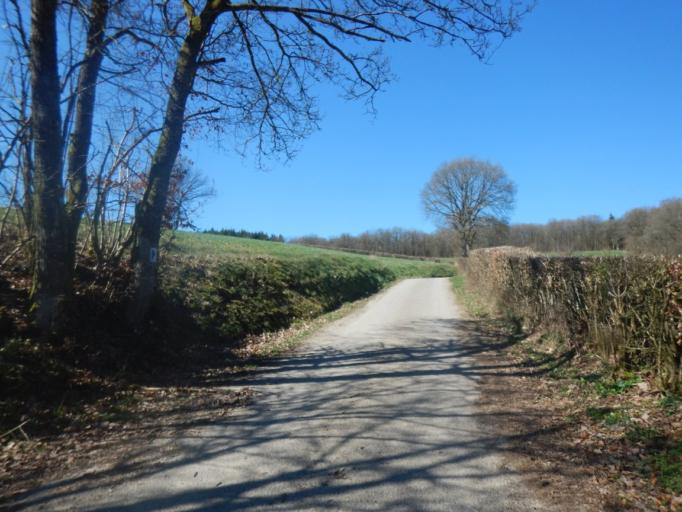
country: LU
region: Diekirch
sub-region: Canton de Wiltz
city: Eschweiler
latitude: 49.9953
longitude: 5.9403
